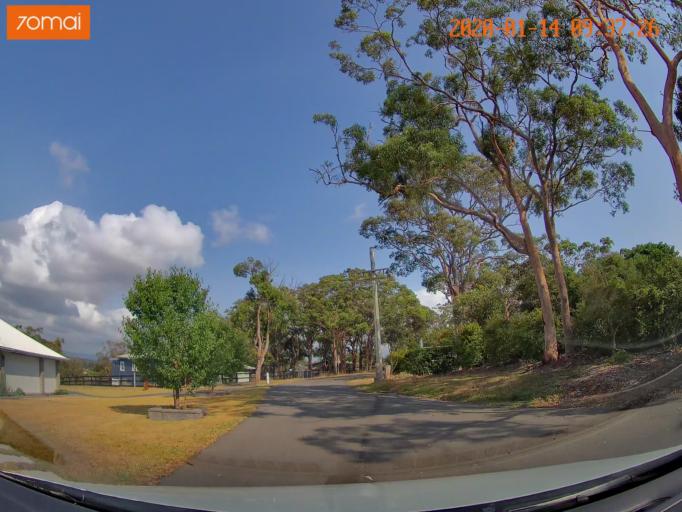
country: AU
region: New South Wales
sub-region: Wyong Shire
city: Kingfisher Shores
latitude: -33.1164
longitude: 151.5598
